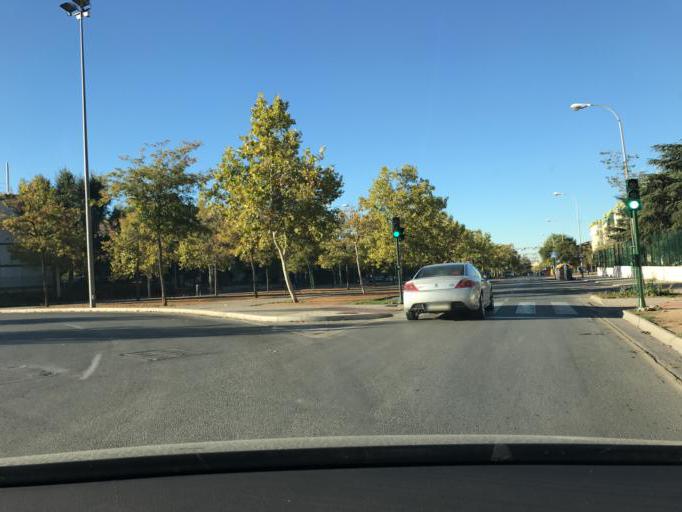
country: ES
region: Andalusia
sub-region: Provincia de Granada
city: Pulianas
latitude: 37.2111
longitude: -3.6100
